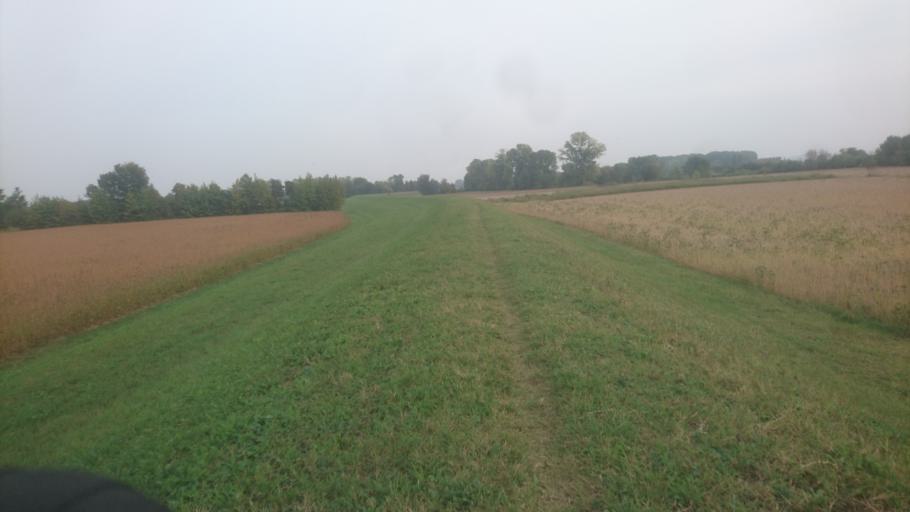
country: IT
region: Veneto
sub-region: Provincia di Padova
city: Cervarese Santa Croce
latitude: 45.4242
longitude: 11.7018
